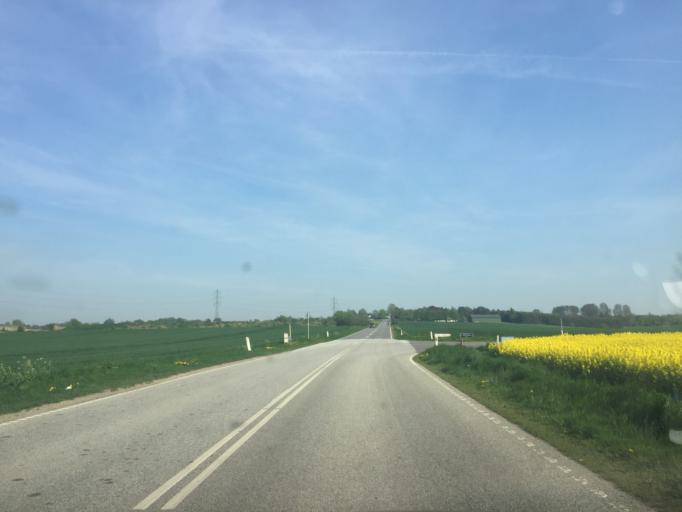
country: DK
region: Capital Region
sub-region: Hoje-Taastrup Kommune
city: Flong
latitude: 55.6730
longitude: 12.2105
